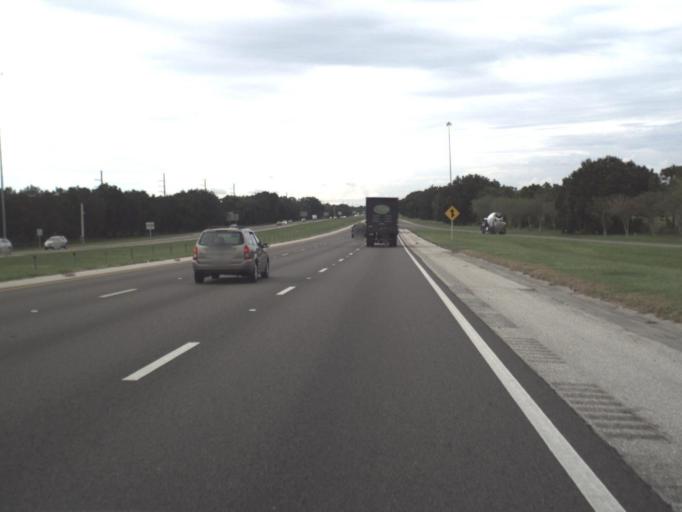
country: US
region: Florida
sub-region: Sarasota County
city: Lake Sarasota
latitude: 27.2676
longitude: -82.4492
